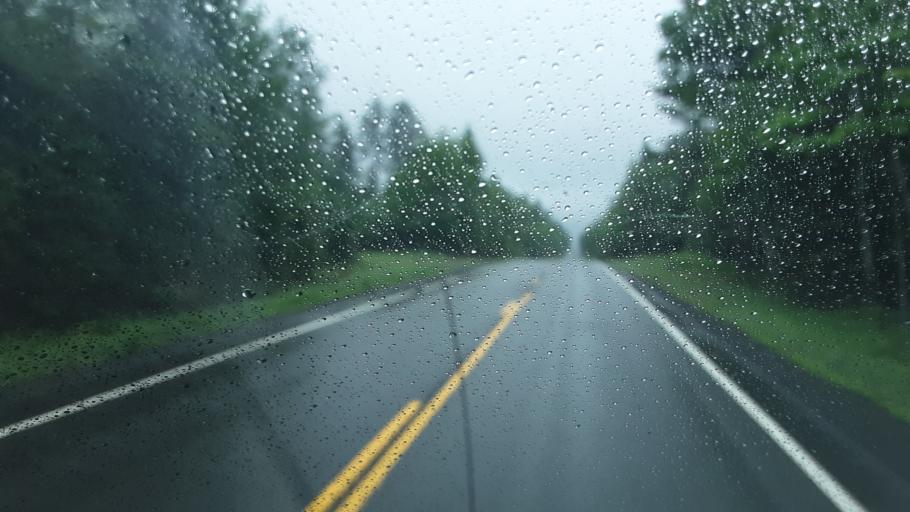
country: US
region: Maine
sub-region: Penobscot County
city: Patten
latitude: 46.3060
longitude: -68.3570
